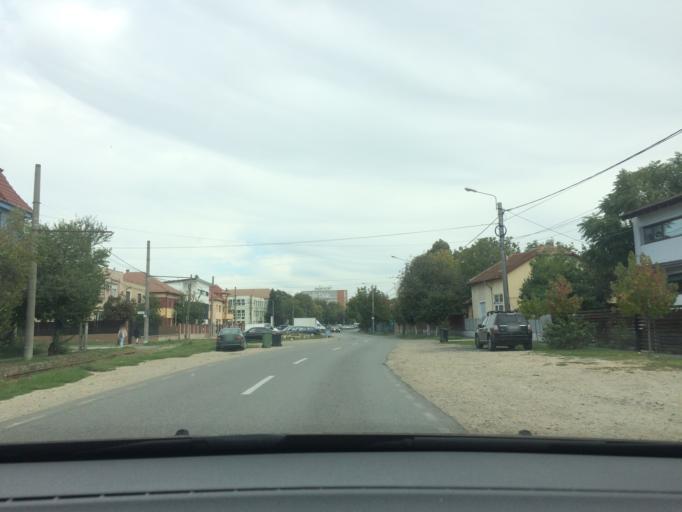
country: RO
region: Timis
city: Timisoara
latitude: 45.7587
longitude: 21.2013
